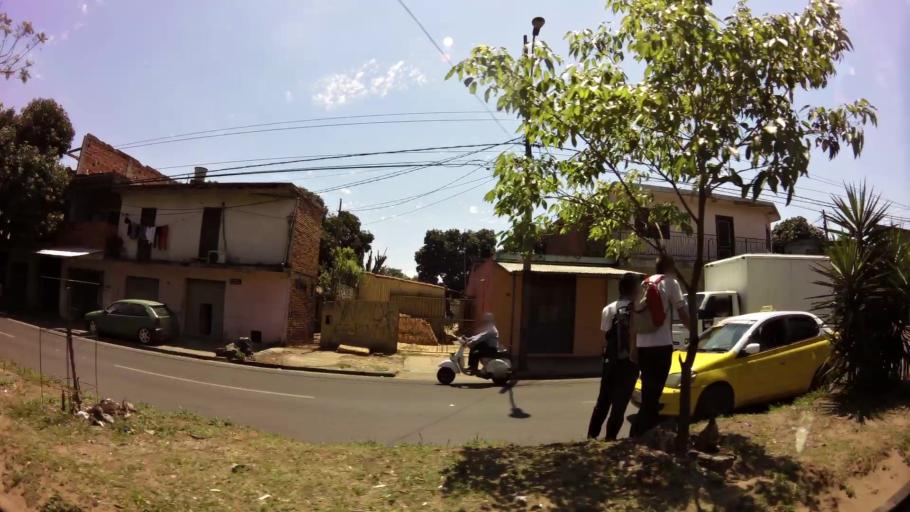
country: PY
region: Central
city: Lambare
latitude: -25.3342
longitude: -57.5784
